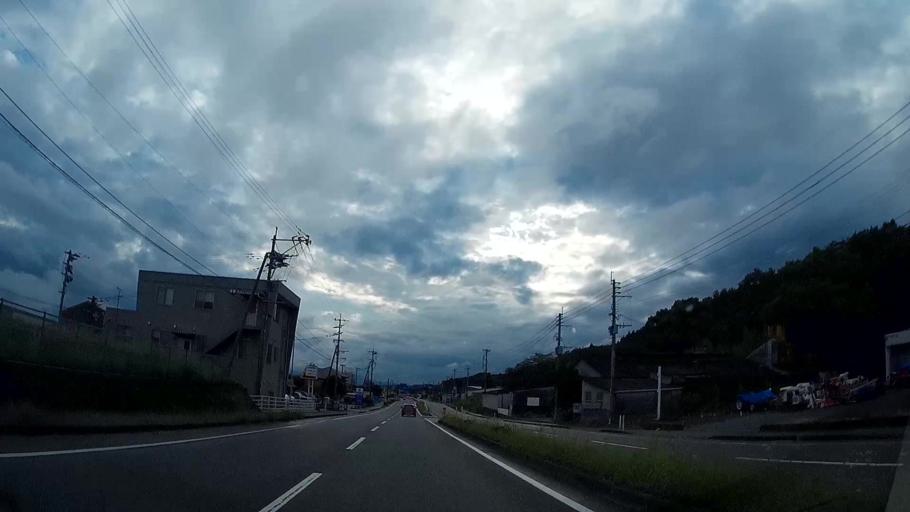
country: JP
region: Kumamoto
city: Ozu
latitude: 32.8803
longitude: 130.8988
